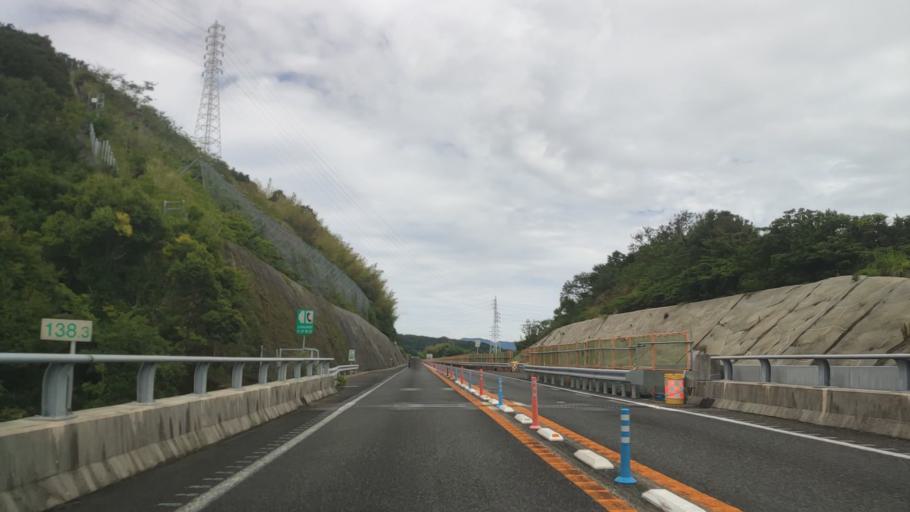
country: JP
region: Wakayama
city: Gobo
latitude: 33.8333
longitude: 135.2200
